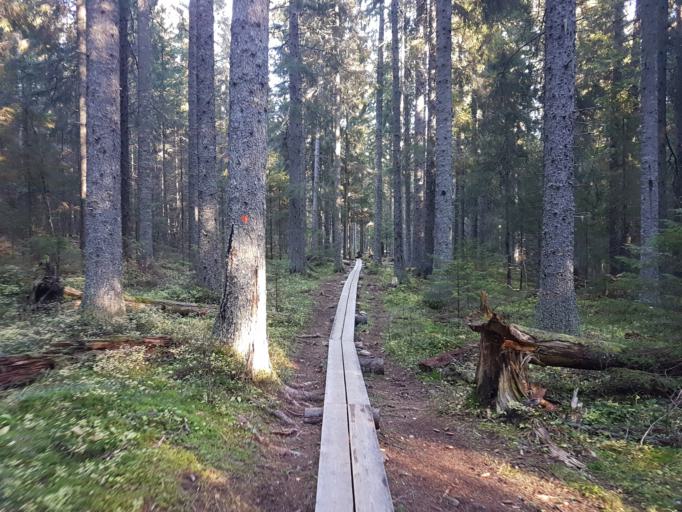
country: SE
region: Vaesternorrland
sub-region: OErnskoeldsviks Kommun
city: Kopmanholmen
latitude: 63.0910
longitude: 18.4973
